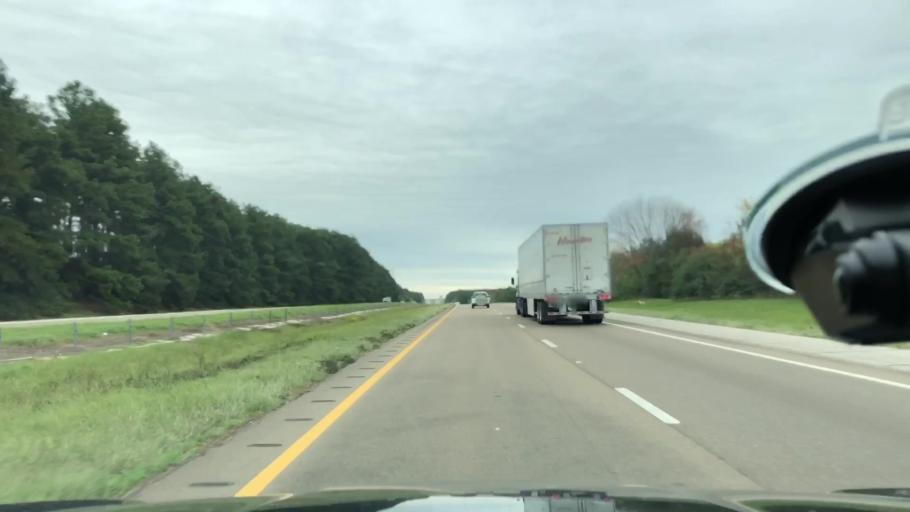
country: US
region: Texas
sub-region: Titus County
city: Mount Pleasant
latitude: 33.1829
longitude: -94.9571
